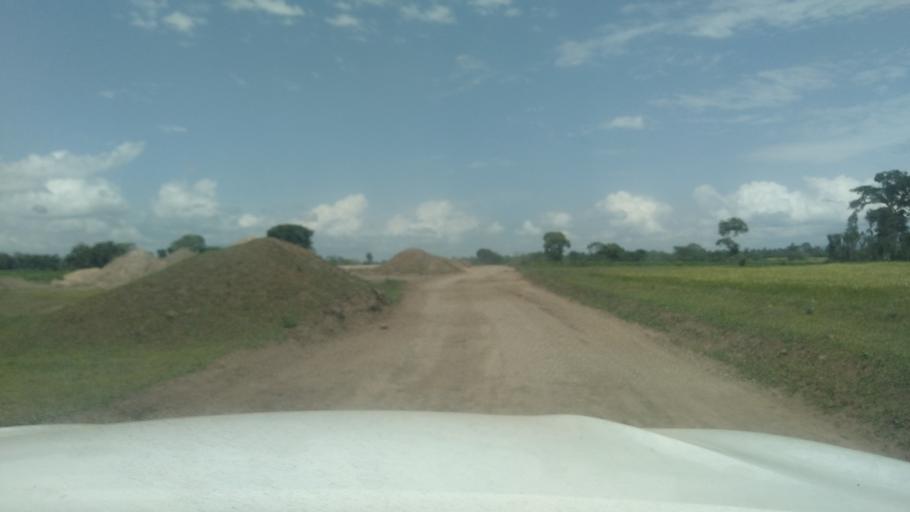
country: ET
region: Oromiya
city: Shashemene
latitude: 7.2737
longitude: 38.6008
